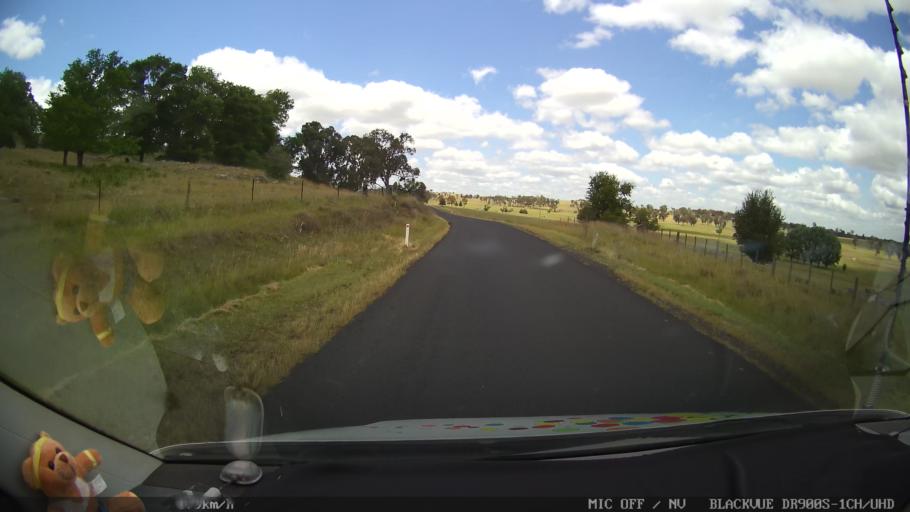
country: AU
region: New South Wales
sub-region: Glen Innes Severn
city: Glen Innes
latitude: -29.4293
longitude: 151.7514
